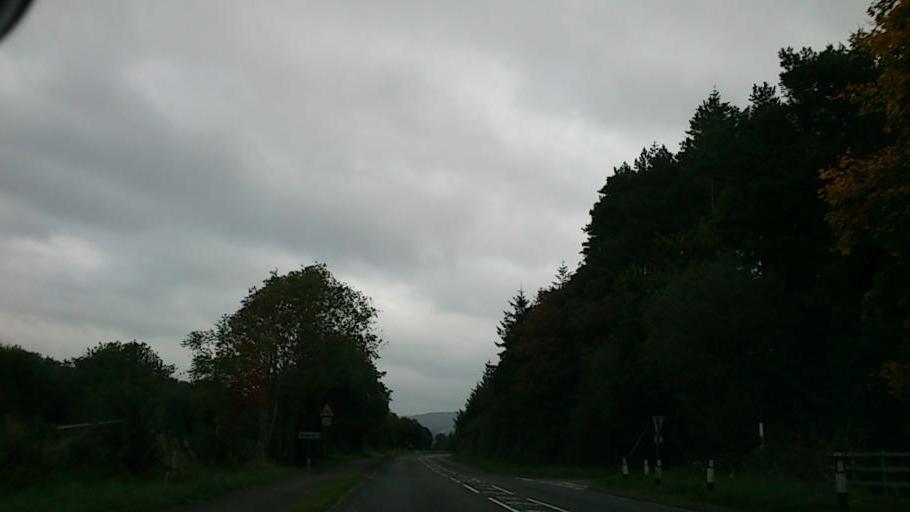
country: GB
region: Wales
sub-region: Sir Powys
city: Machynlleth
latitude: 52.5801
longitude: -3.8783
